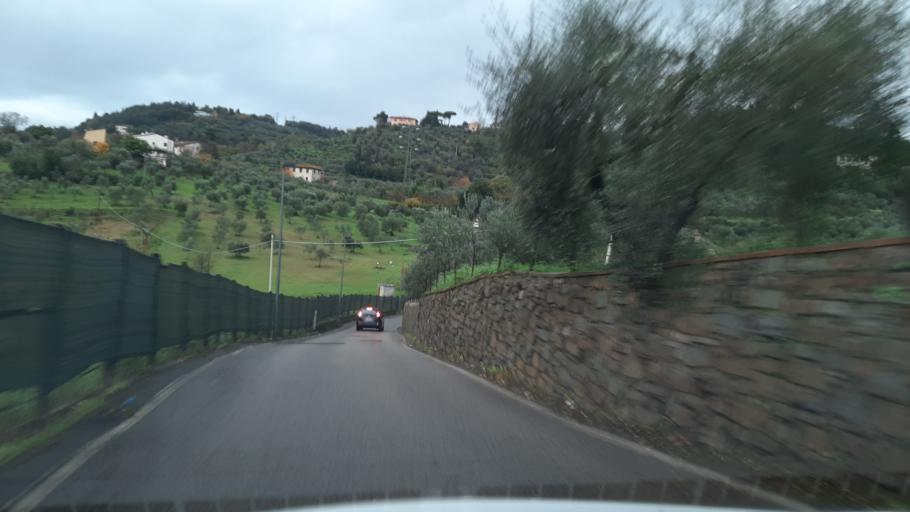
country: IT
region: Tuscany
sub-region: Province of Florence
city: Fiesole
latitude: 43.8052
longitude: 11.2687
